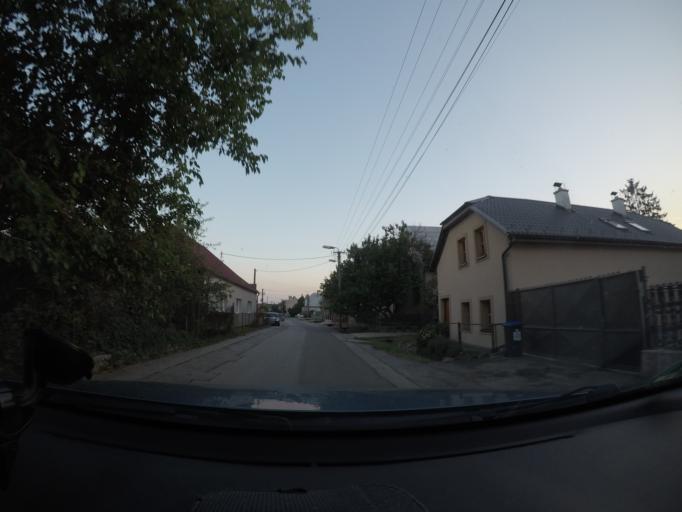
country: SK
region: Trenciansky
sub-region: Okres Nove Mesto nad Vahom
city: Nove Mesto nad Vahom
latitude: 48.8309
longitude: 17.9050
